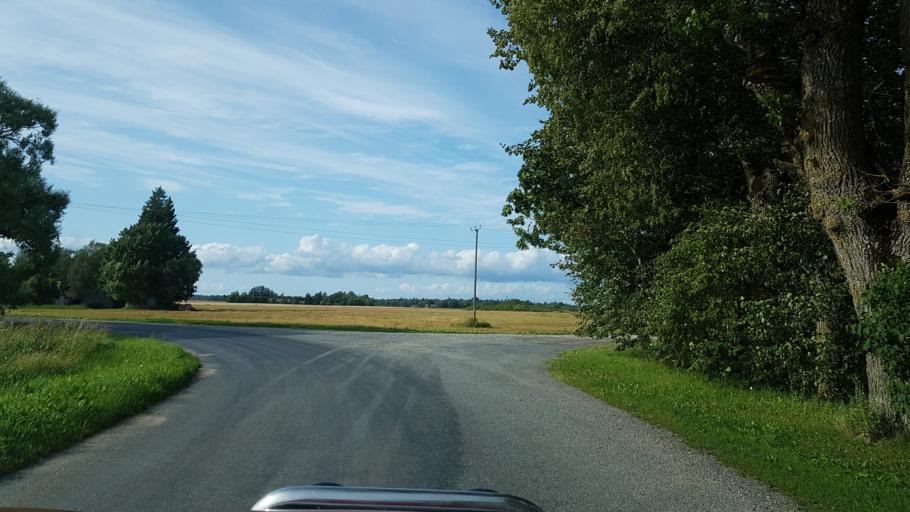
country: EE
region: Laeaene
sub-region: Lihula vald
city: Lihula
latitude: 58.4476
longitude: 24.0018
